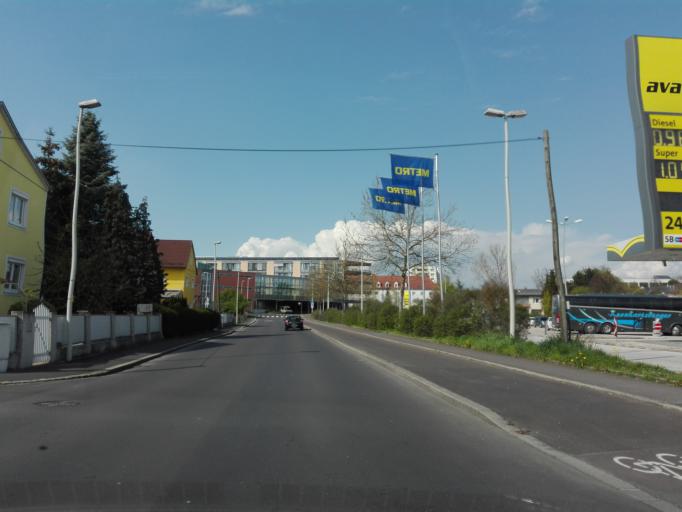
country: AT
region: Upper Austria
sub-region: Politischer Bezirk Linz-Land
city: Ansfelden
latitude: 48.2480
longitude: 14.2940
